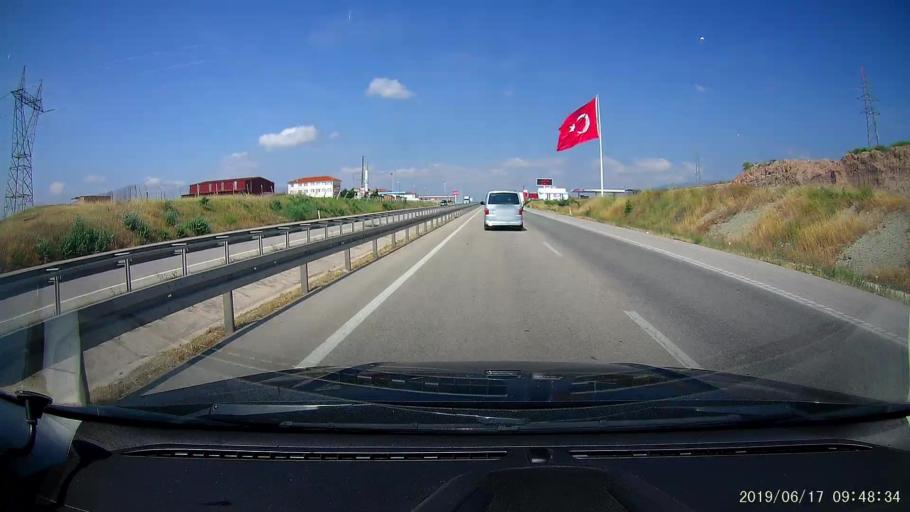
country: TR
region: Amasya
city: Merzifon
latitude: 40.8743
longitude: 35.5495
